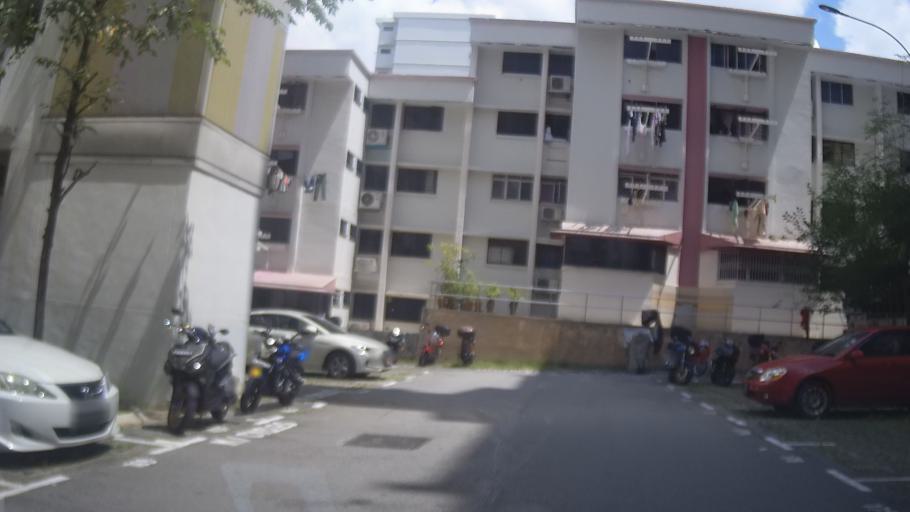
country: MY
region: Johor
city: Johor Bahru
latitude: 1.4334
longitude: 103.7776
